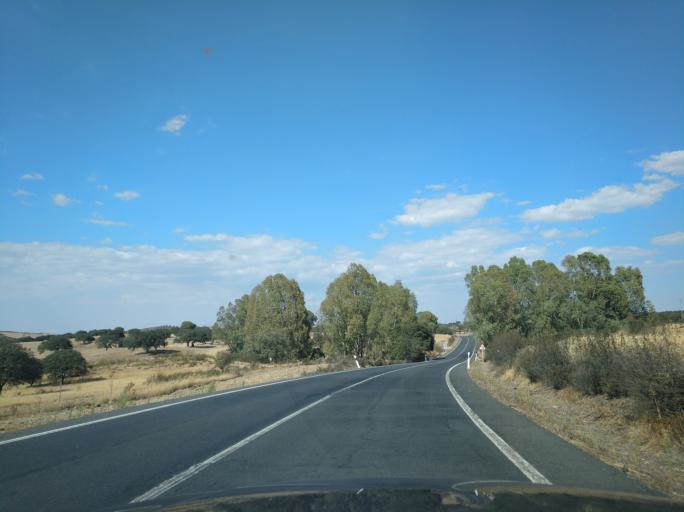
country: ES
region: Andalusia
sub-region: Provincia de Huelva
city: Cabezas Rubias
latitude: 37.6574
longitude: -7.1179
